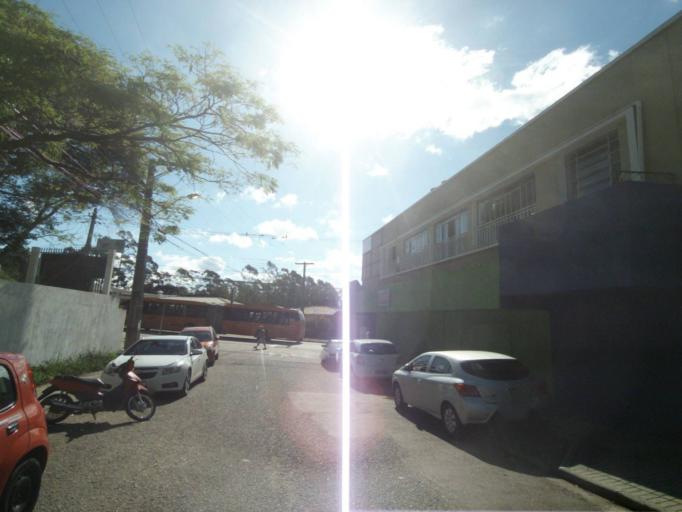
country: BR
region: Parana
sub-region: Curitiba
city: Curitiba
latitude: -25.3910
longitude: -49.2603
